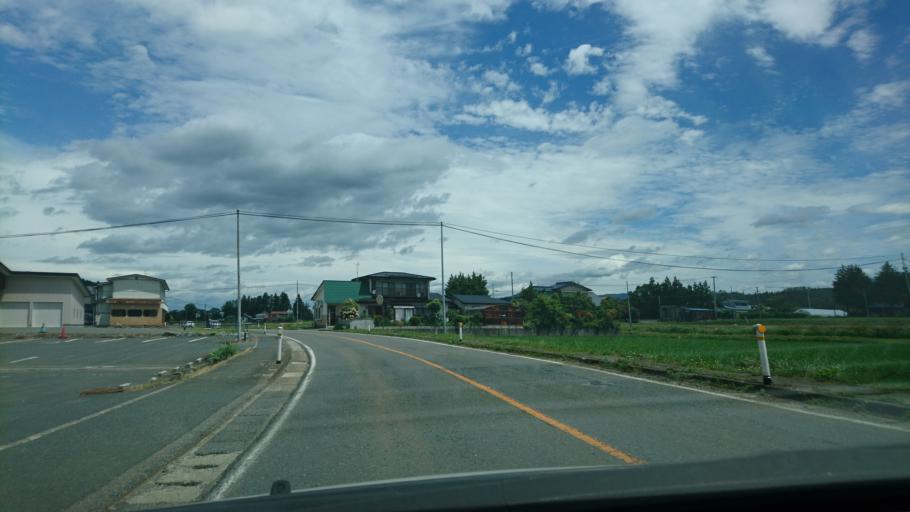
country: JP
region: Iwate
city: Morioka-shi
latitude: 39.5528
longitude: 141.1783
